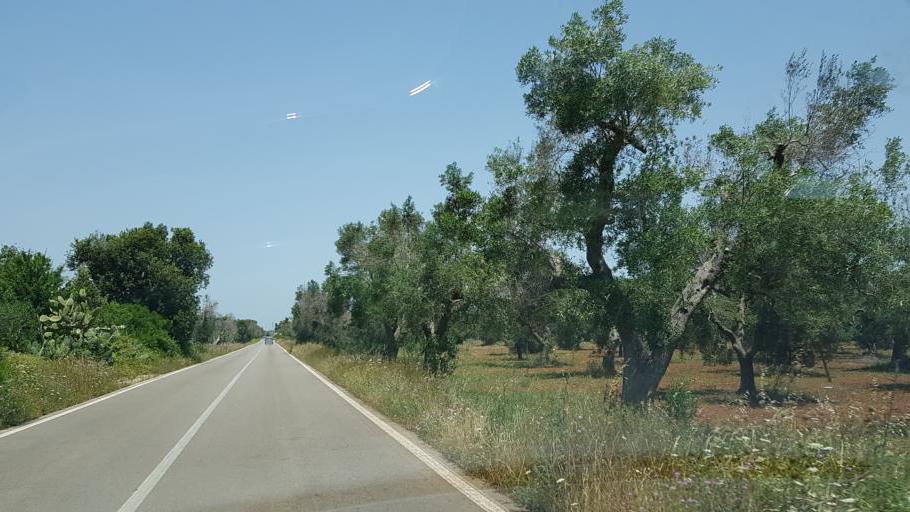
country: IT
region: Apulia
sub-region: Provincia di Lecce
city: Veglie
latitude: 40.3208
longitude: 17.9238
